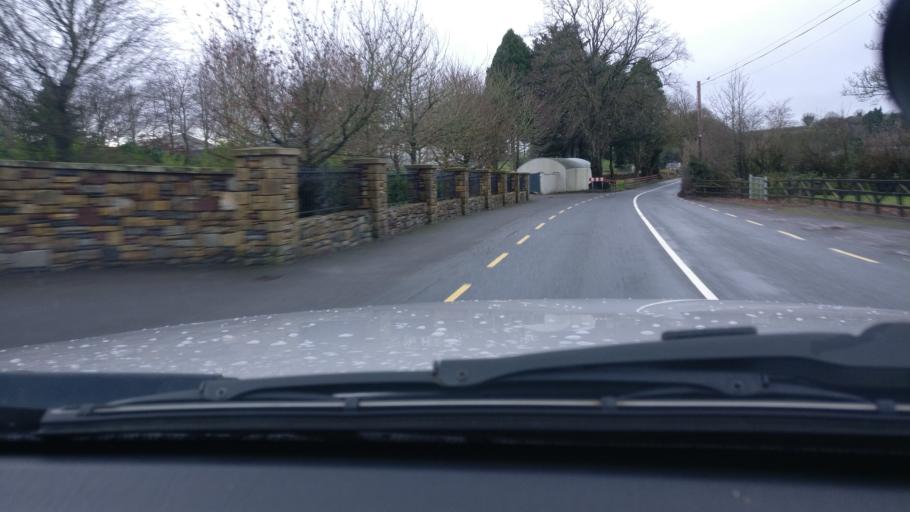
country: IE
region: Leinster
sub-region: An Longfort
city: Granard
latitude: 53.8071
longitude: -7.3769
